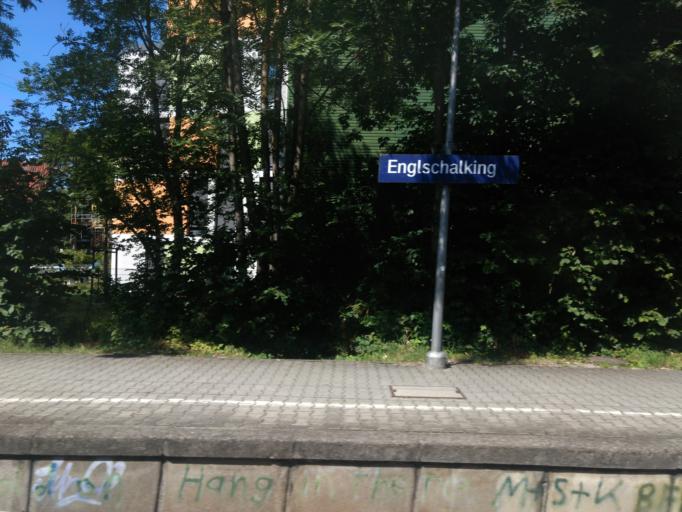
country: DE
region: Bavaria
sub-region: Upper Bavaria
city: Bogenhausen
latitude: 48.1598
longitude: 11.6480
